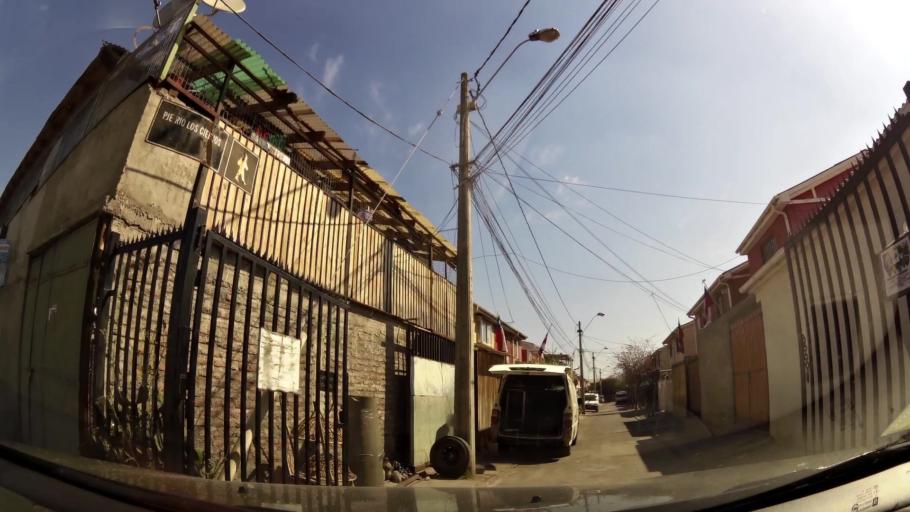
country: CL
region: Santiago Metropolitan
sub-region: Provincia de Cordillera
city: Puente Alto
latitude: -33.6296
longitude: -70.6122
